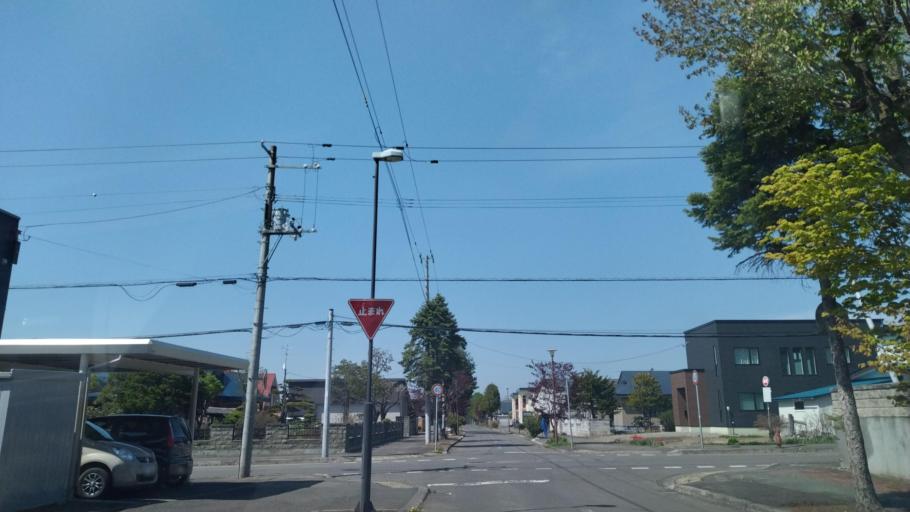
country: JP
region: Hokkaido
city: Obihiro
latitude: 42.9125
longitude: 143.0450
